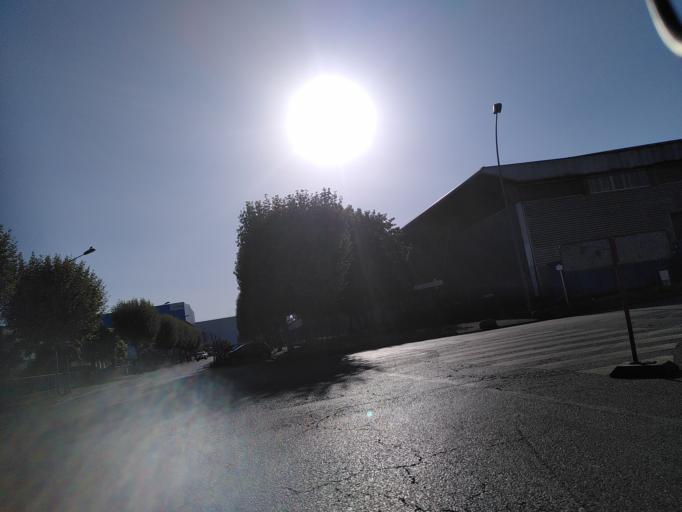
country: FR
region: Ile-de-France
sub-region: Departement du Val-de-Marne
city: Vitry-sur-Seine
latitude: 48.7938
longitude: 2.4138
